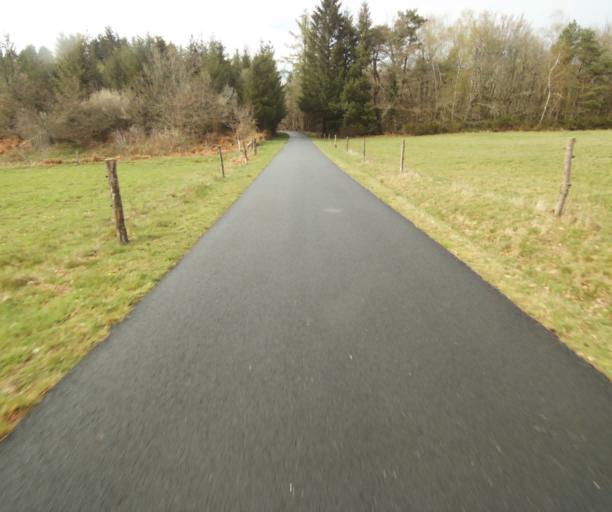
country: FR
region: Limousin
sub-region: Departement de la Correze
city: Saint-Privat
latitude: 45.2296
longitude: 2.0023
